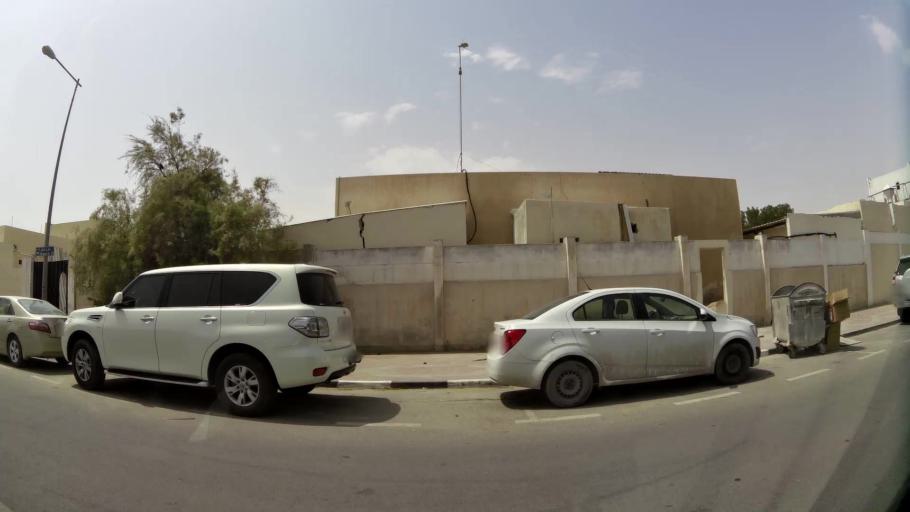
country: QA
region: Baladiyat ar Rayyan
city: Ar Rayyan
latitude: 25.2434
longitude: 51.4262
